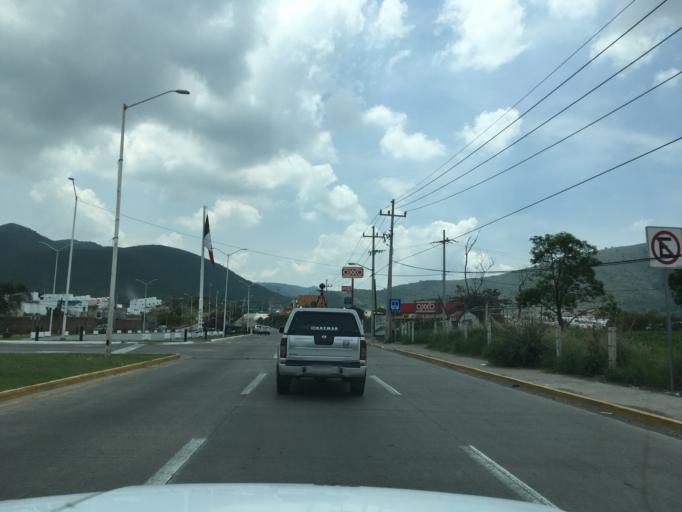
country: MX
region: Jalisco
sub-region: Tlajomulco de Zuniga
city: Santa Cruz de las Flores
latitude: 20.4902
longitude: -103.4884
